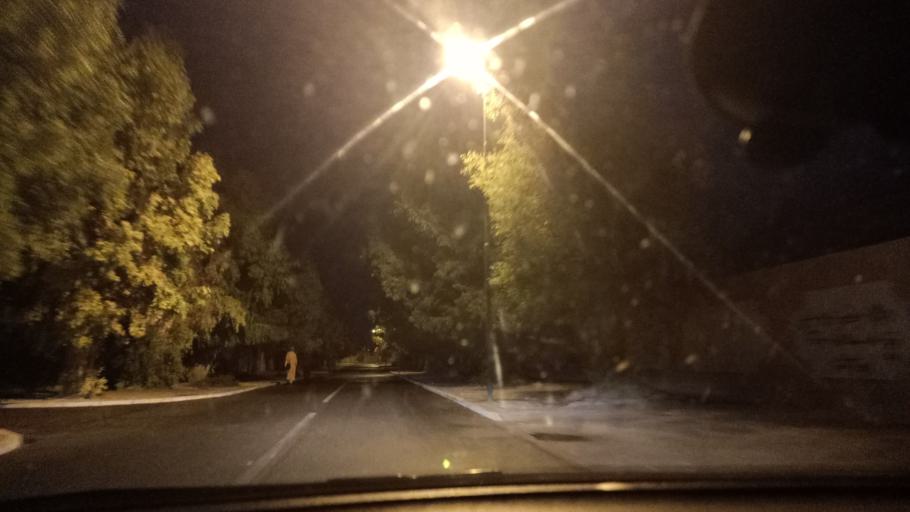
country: MA
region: Doukkala-Abda
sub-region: Safi
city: Youssoufia
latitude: 32.2479
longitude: -8.5311
